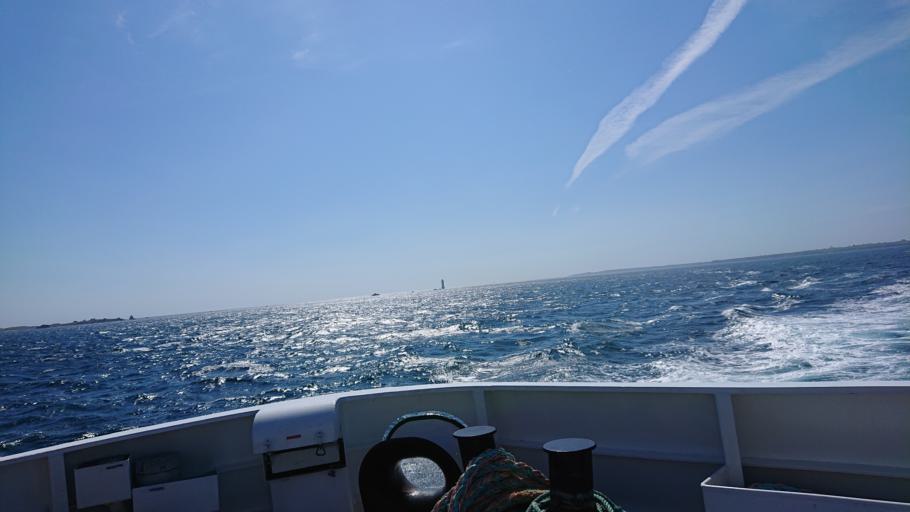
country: FR
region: Brittany
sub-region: Departement du Finistere
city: Lampaul-Plouarzel
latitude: 48.4447
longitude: -4.9922
